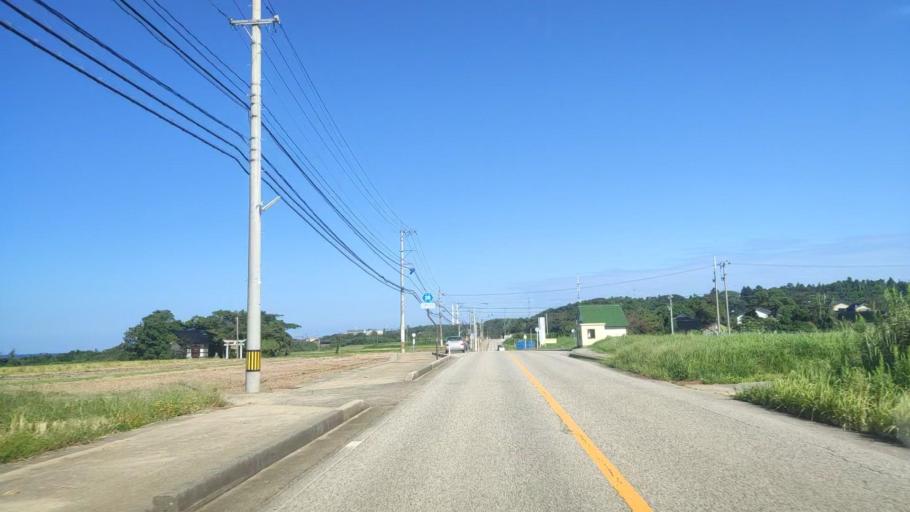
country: JP
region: Ishikawa
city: Hakui
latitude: 37.0450
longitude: 136.7388
